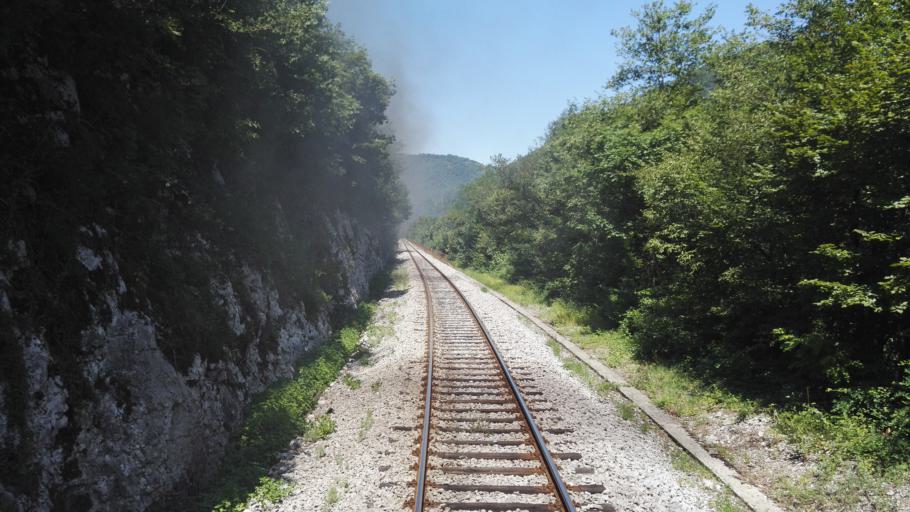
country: SI
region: Nova Gorica
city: Solkan
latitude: 46.0058
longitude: 13.6253
